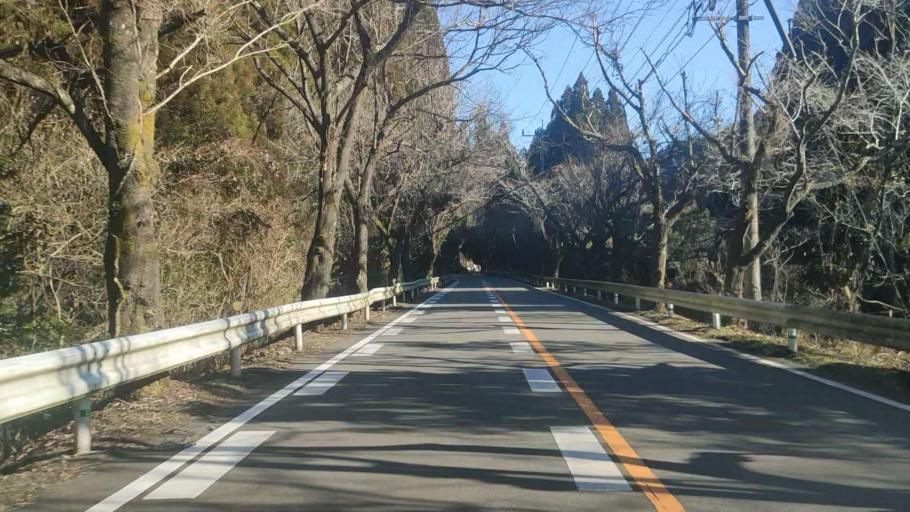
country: JP
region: Miyazaki
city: Nobeoka
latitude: 32.6393
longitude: 131.7432
